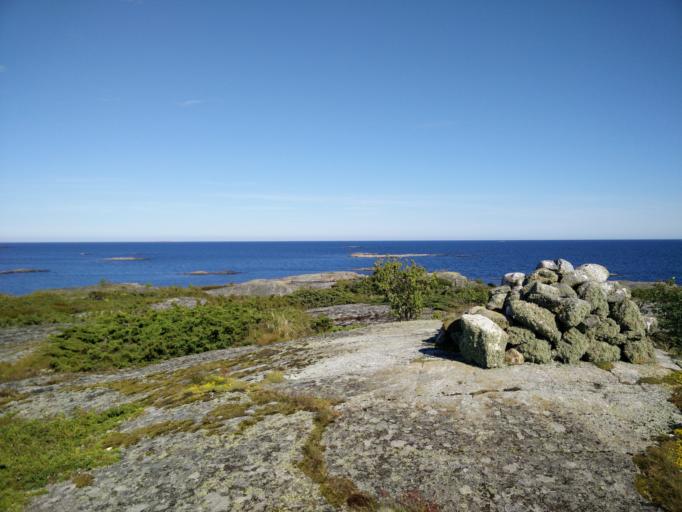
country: SE
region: Stockholm
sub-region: Norrtalje Kommun
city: Bjorko
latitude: 59.4094
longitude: 19.3409
